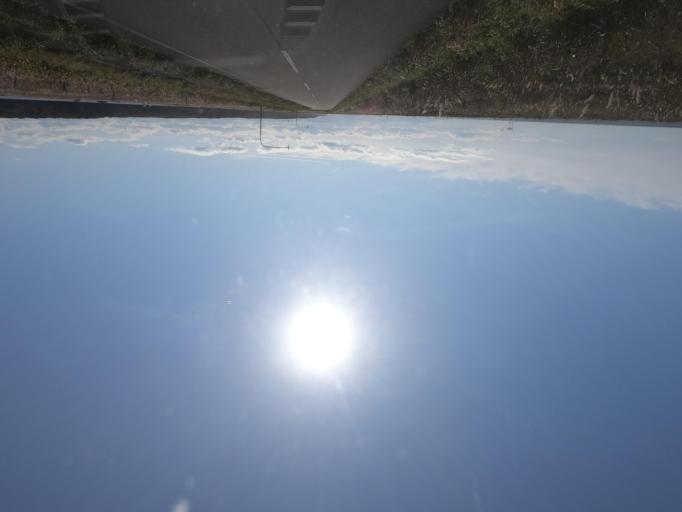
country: JP
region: Hokkaido
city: Obihiro
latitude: 42.5912
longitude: 143.5410
